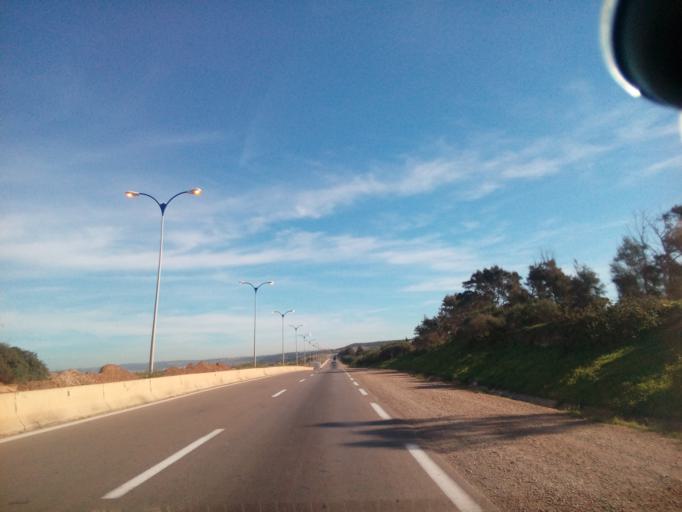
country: DZ
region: Mostaganem
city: Mostaganem
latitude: 35.8025
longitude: -0.0659
